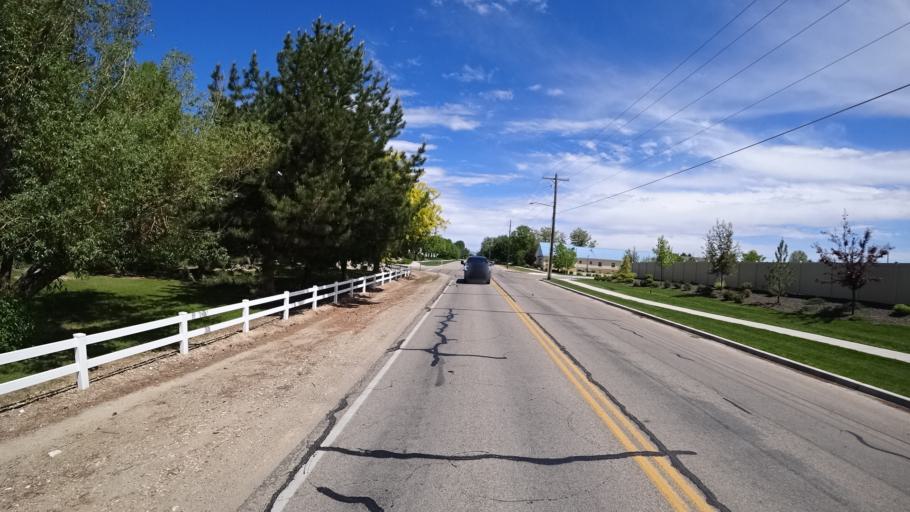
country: US
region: Idaho
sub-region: Ada County
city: Meridian
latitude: 43.5757
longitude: -116.3812
